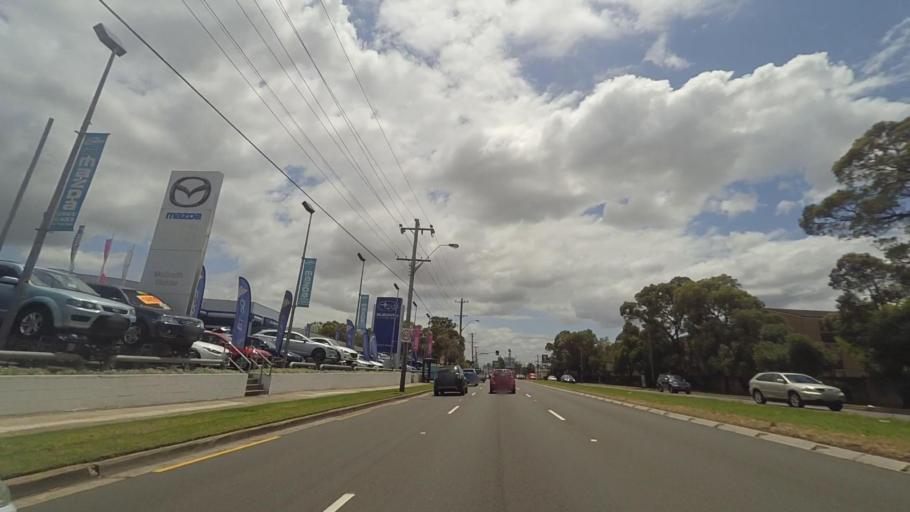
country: AU
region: New South Wales
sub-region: Liverpool
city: Miller
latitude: -33.9333
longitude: 150.9164
